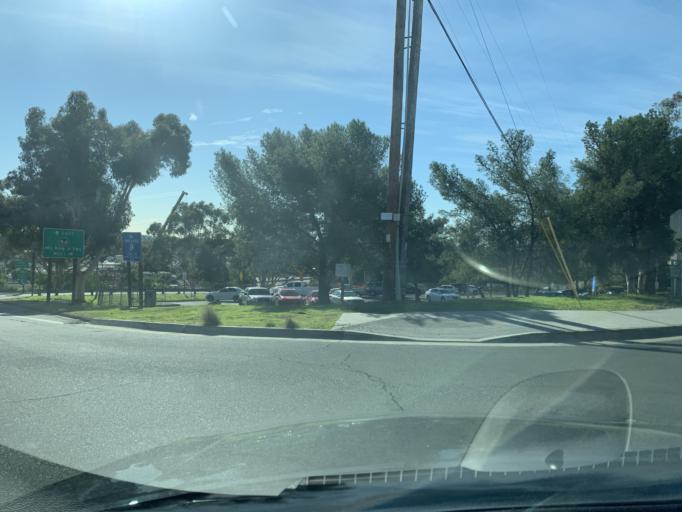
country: US
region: California
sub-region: San Diego County
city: Lemon Grove
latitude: 32.7480
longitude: -117.0314
